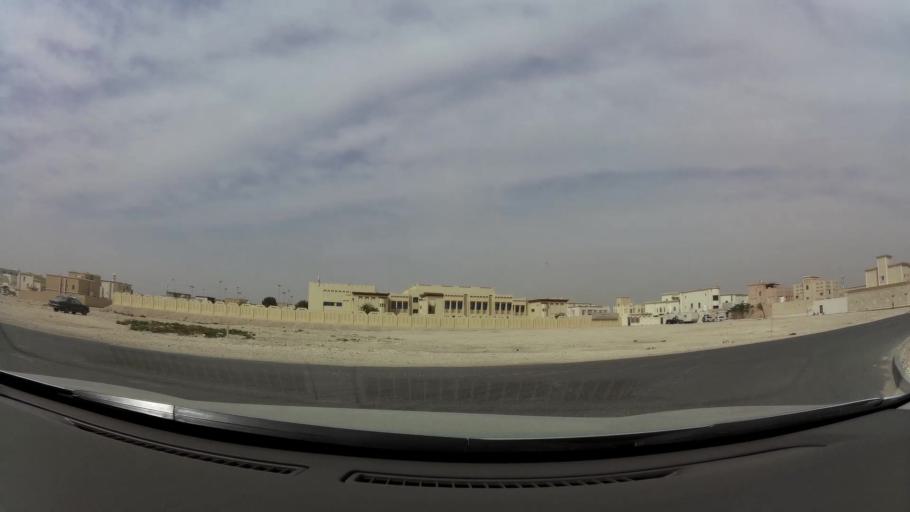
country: QA
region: Baladiyat ad Dawhah
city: Doha
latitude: 25.2113
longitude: 51.4897
